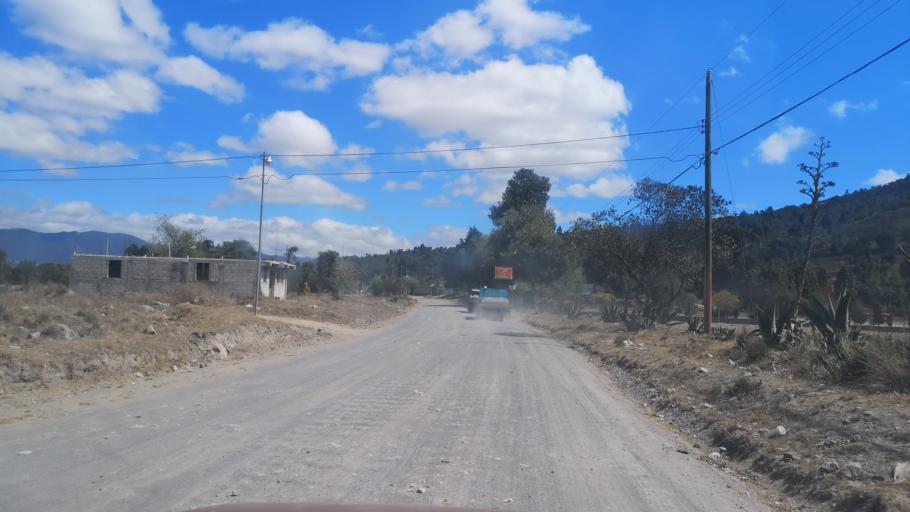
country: GT
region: Quetzaltenango
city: Quetzaltenango
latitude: 14.8055
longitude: -91.5358
